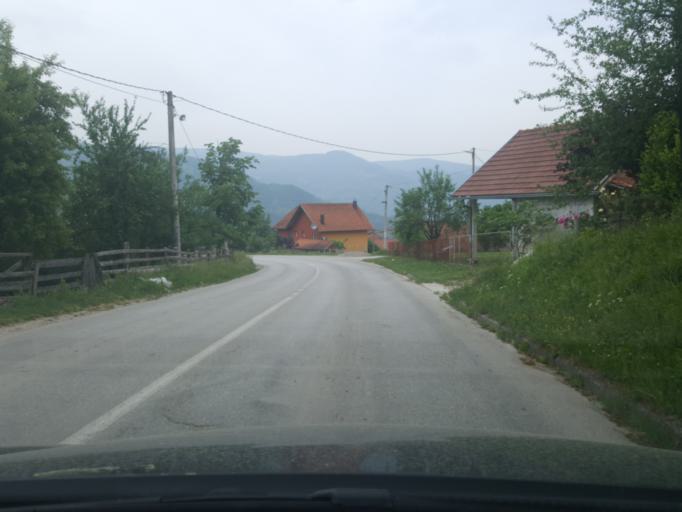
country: RS
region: Central Serbia
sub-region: Zlatiborski Okrug
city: Bajina Basta
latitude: 43.9631
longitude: 19.5509
